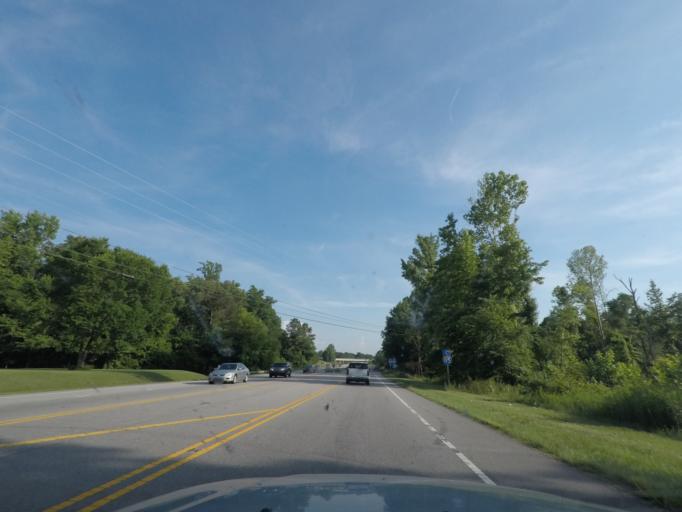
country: US
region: North Carolina
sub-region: Granville County
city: Oxford
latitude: 36.2755
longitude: -78.6075
